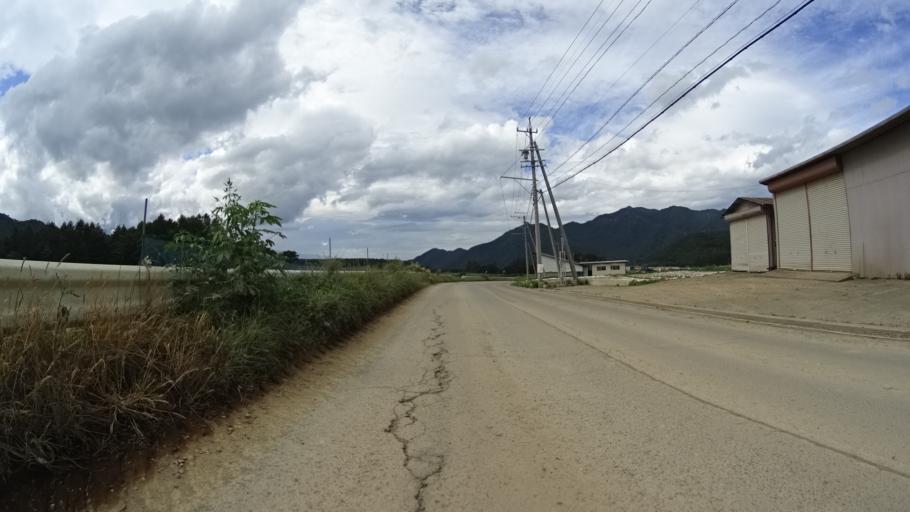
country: JP
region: Yamanashi
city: Nirasaki
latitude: 35.9520
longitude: 138.5475
